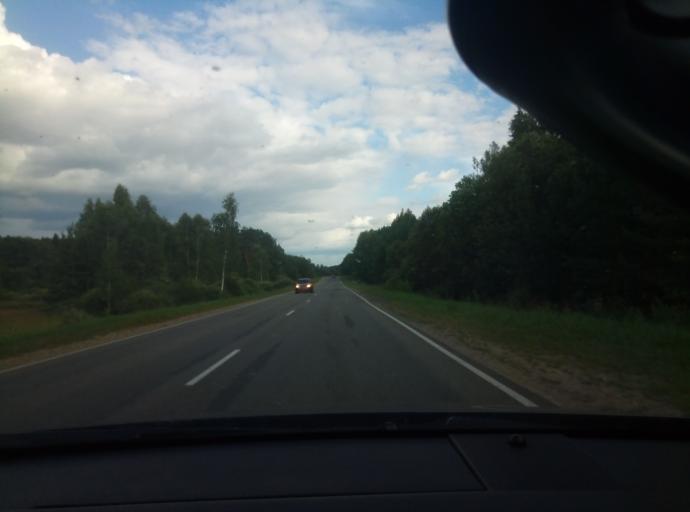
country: RU
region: Kaluga
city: Nikola-Lenivets
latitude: 54.5406
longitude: 35.5456
